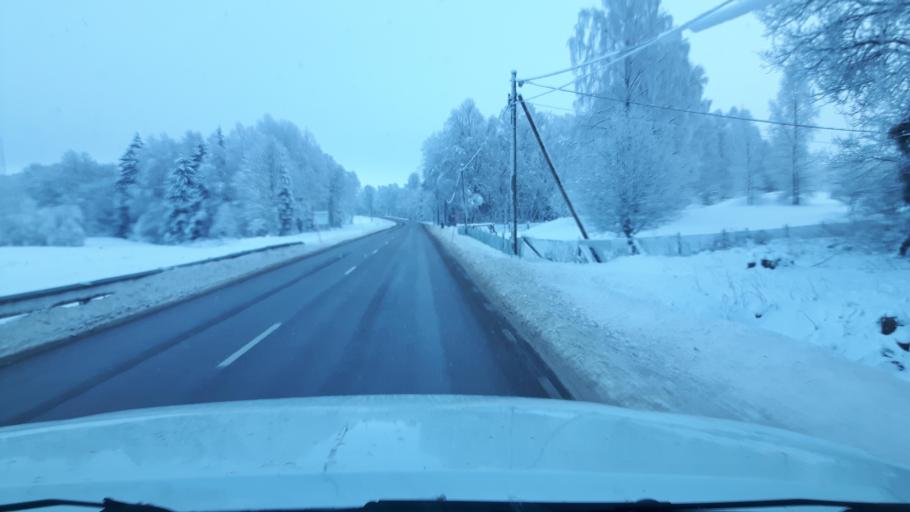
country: SE
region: Halland
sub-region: Kungsbacka Kommun
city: Fjaeras kyrkby
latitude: 57.4000
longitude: 12.2332
